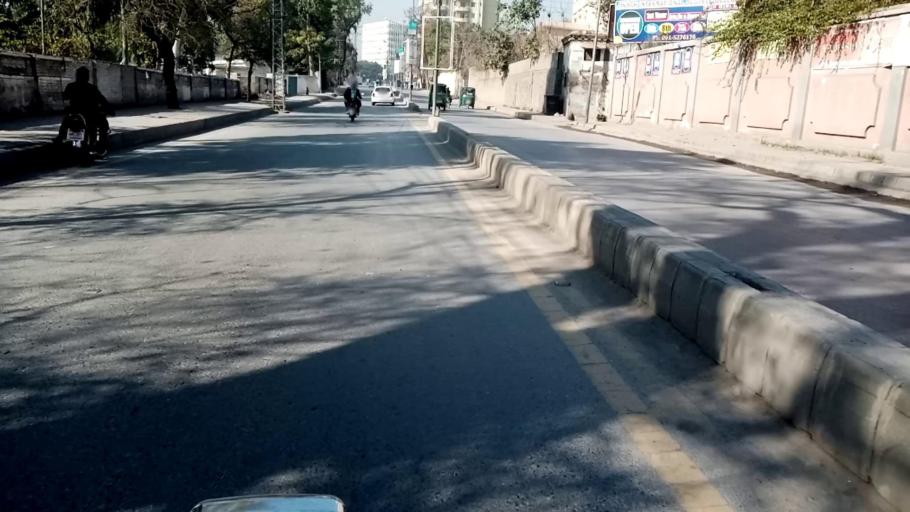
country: PK
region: Khyber Pakhtunkhwa
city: Peshawar
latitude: 34.0027
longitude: 71.5486
